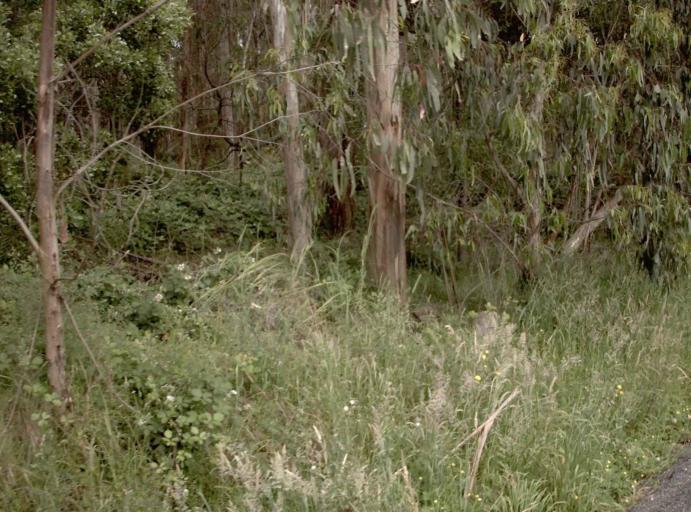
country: AU
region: Victoria
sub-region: Latrobe
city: Moe
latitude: -37.9651
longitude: 146.1347
